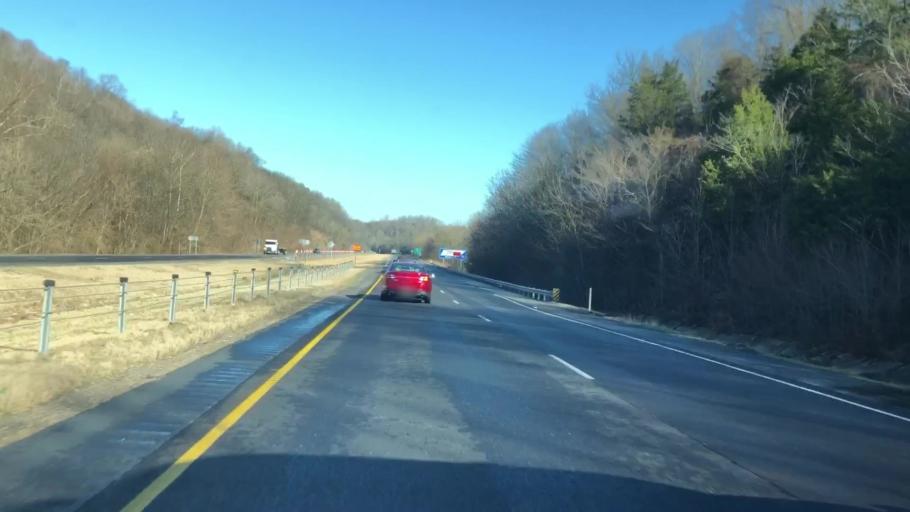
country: US
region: Alabama
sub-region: Limestone County
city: Ardmore
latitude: 34.9920
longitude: -86.8790
